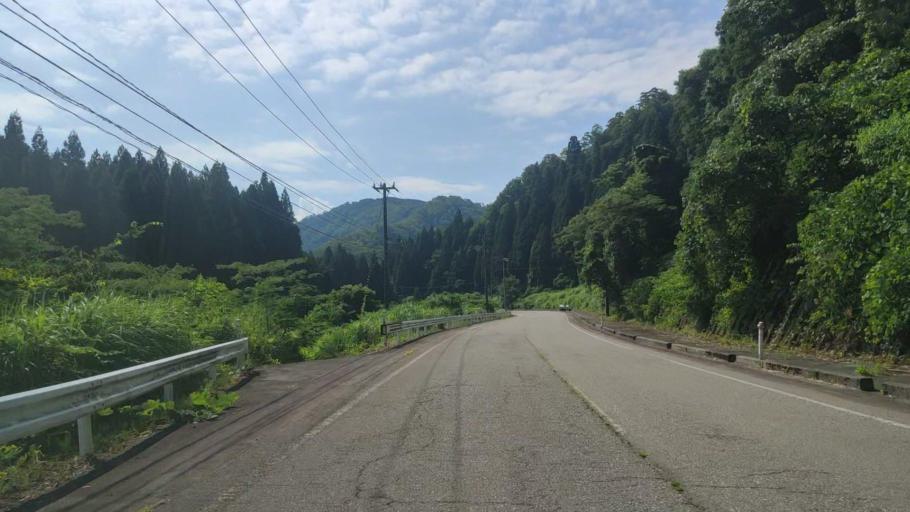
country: JP
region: Ishikawa
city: Komatsu
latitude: 36.3246
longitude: 136.5296
